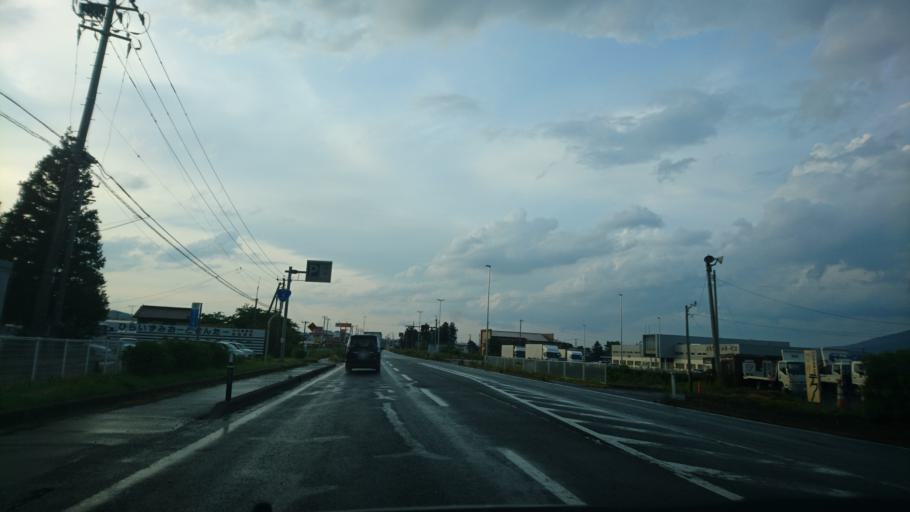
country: JP
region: Iwate
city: Ichinoseki
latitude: 38.9663
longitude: 141.1200
